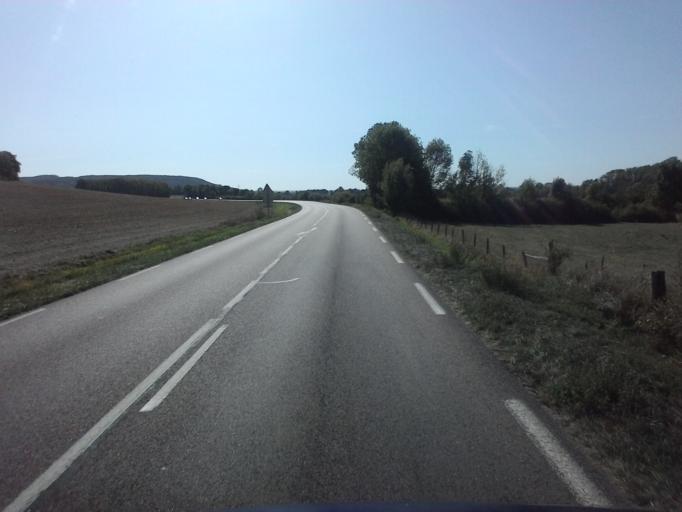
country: FR
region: Champagne-Ardenne
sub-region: Departement de l'Aube
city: Mussy-sur-Seine
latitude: 47.9285
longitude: 4.5432
